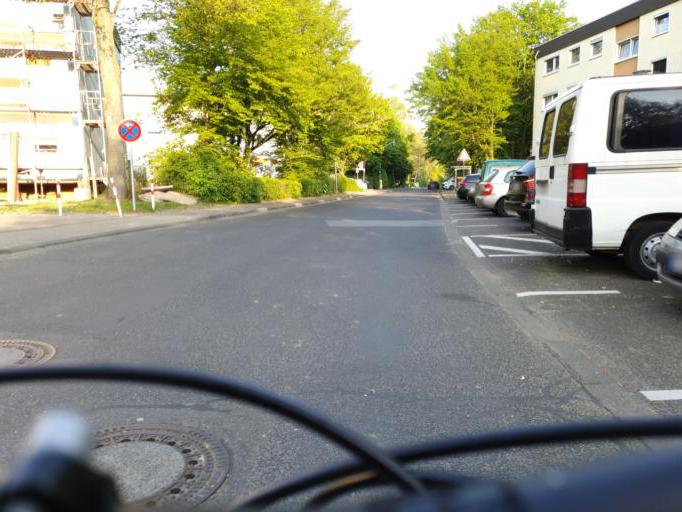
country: DE
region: North Rhine-Westphalia
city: Opladen
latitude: 51.0490
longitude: 7.0568
